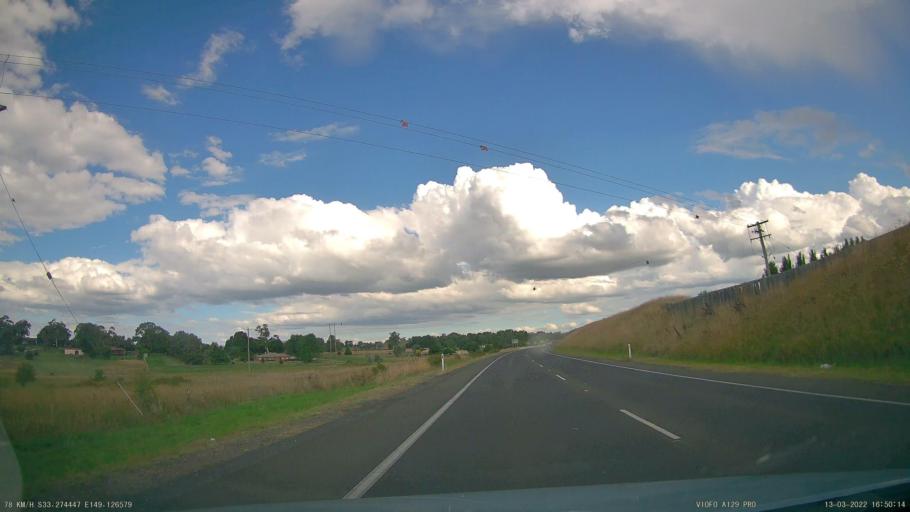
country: AU
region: New South Wales
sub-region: Orange Municipality
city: Orange
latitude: -33.2746
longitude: 149.1267
